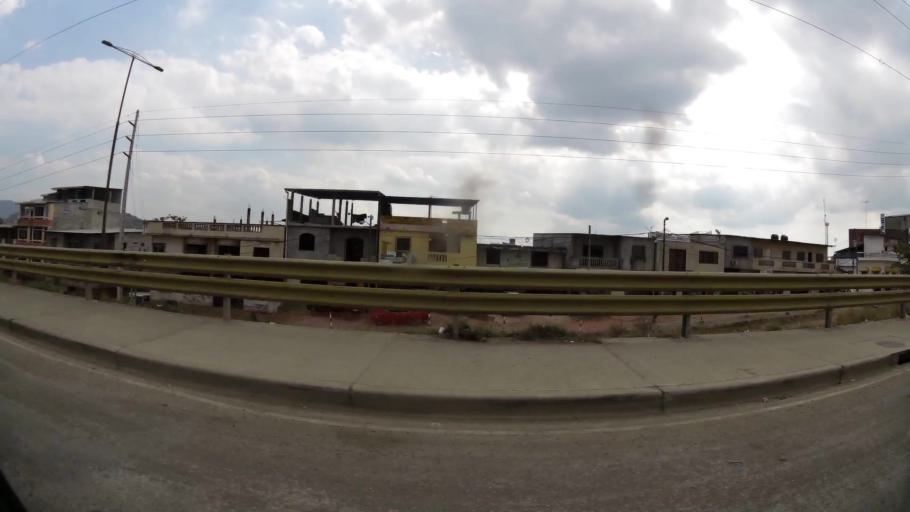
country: EC
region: Guayas
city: Santa Lucia
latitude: -2.1143
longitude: -79.9479
